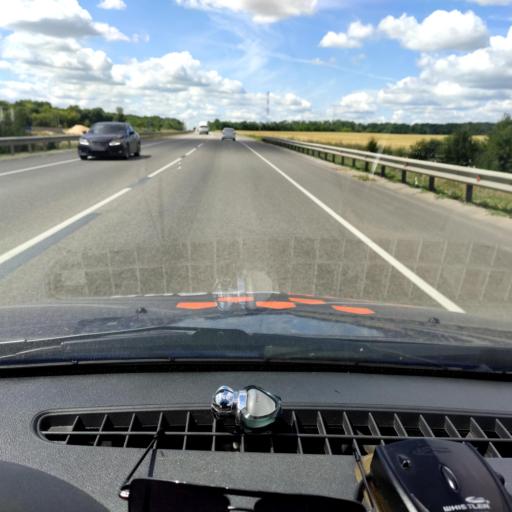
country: RU
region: Lipetsk
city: Borinskoye
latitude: 52.4684
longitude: 39.3450
